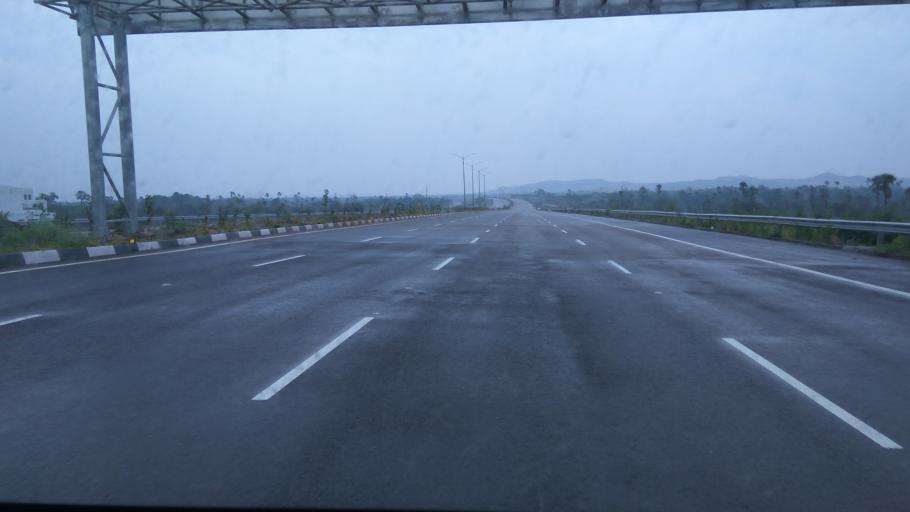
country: IN
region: Telangana
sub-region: Rangareddi
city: Ghatkesar
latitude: 17.4541
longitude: 78.6689
